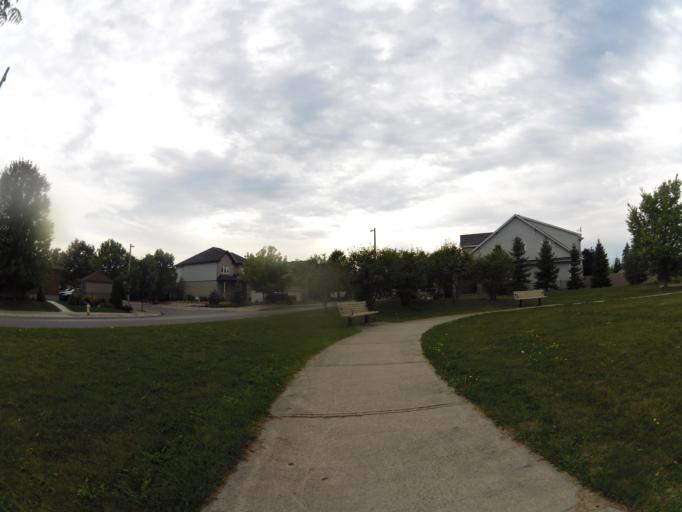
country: CA
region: Ontario
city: Bells Corners
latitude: 45.2762
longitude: -75.9325
